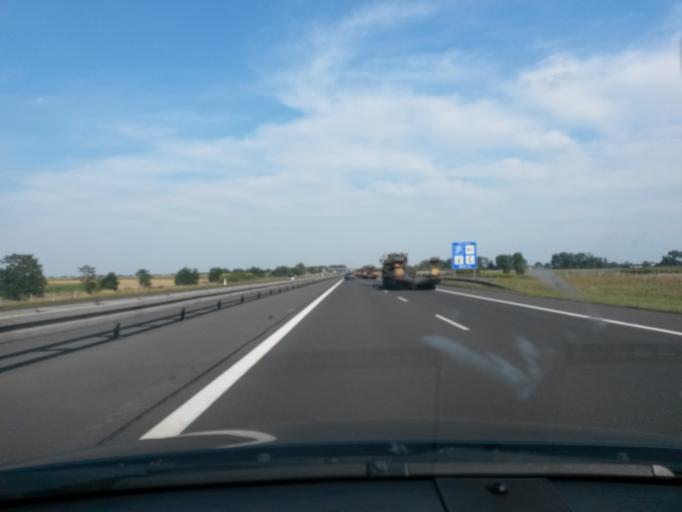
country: PL
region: Greater Poland Voivodeship
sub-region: Powiat wrzesinski
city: Wrzesnia
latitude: 52.2976
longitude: 17.6387
